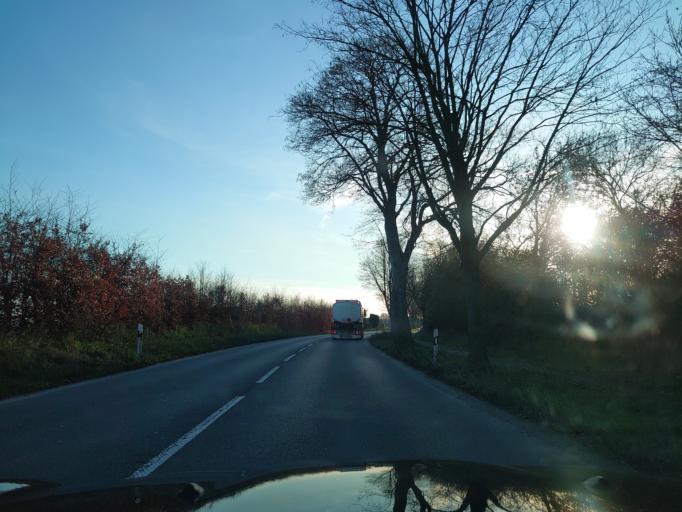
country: DE
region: North Rhine-Westphalia
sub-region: Regierungsbezirk Dusseldorf
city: Rommerskirchen
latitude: 51.0609
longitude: 6.7197
